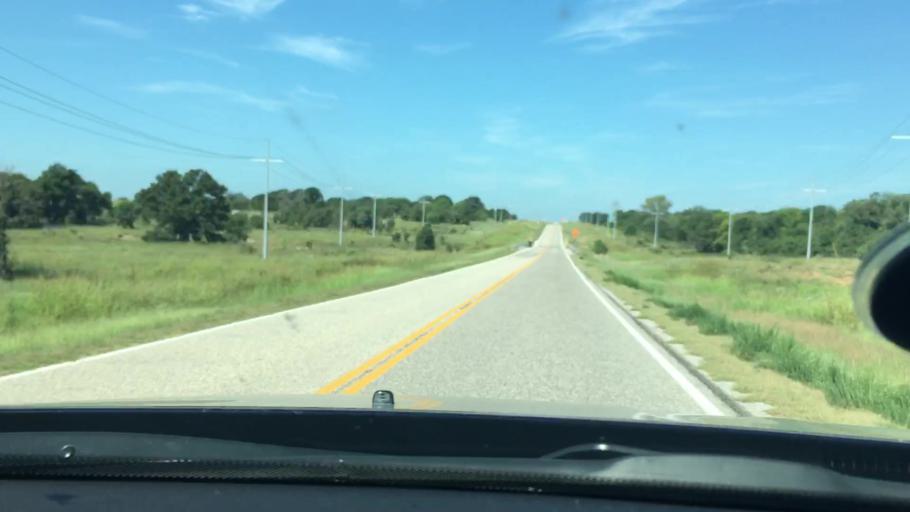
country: US
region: Oklahoma
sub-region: Johnston County
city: Tishomingo
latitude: 34.3613
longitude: -96.6207
